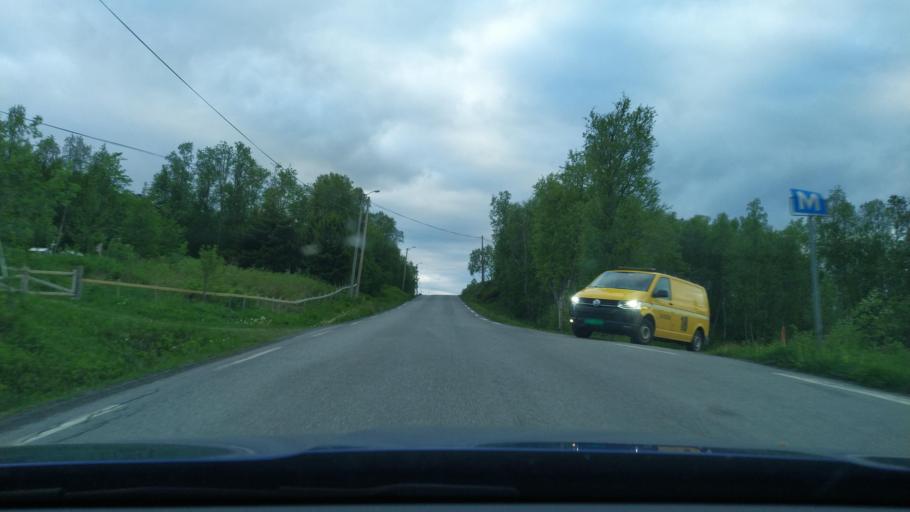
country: NO
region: Troms
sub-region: Tranoy
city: Vangsvika
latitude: 69.1285
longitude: 17.8624
